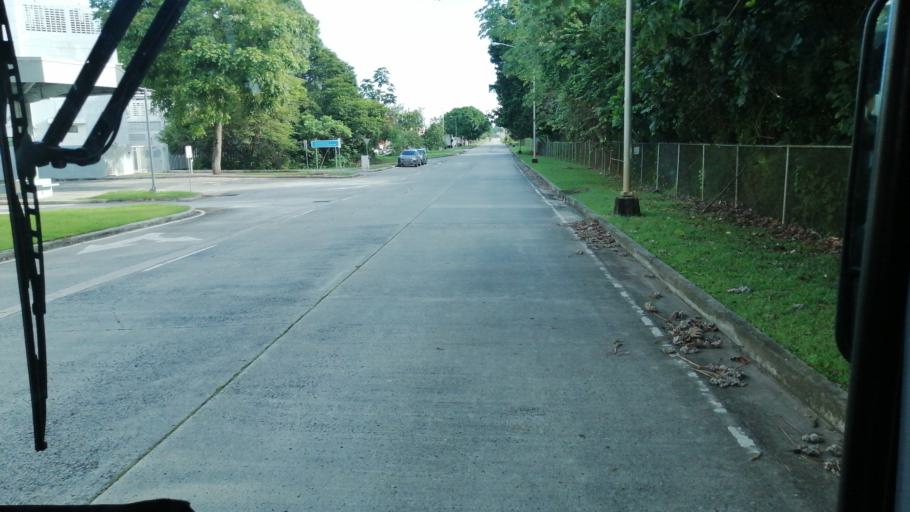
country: PA
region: Panama
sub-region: Distrito de Panama
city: Ancon
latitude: 8.9264
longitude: -79.5943
